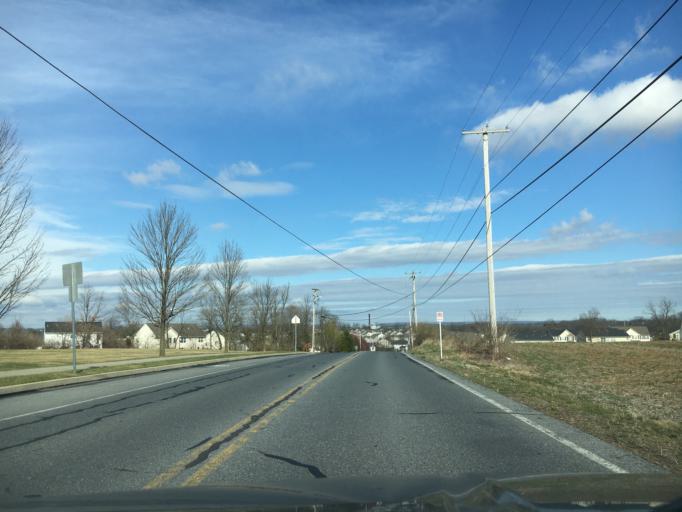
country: US
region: Pennsylvania
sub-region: Northampton County
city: North Catasauqua
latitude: 40.6813
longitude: -75.4647
